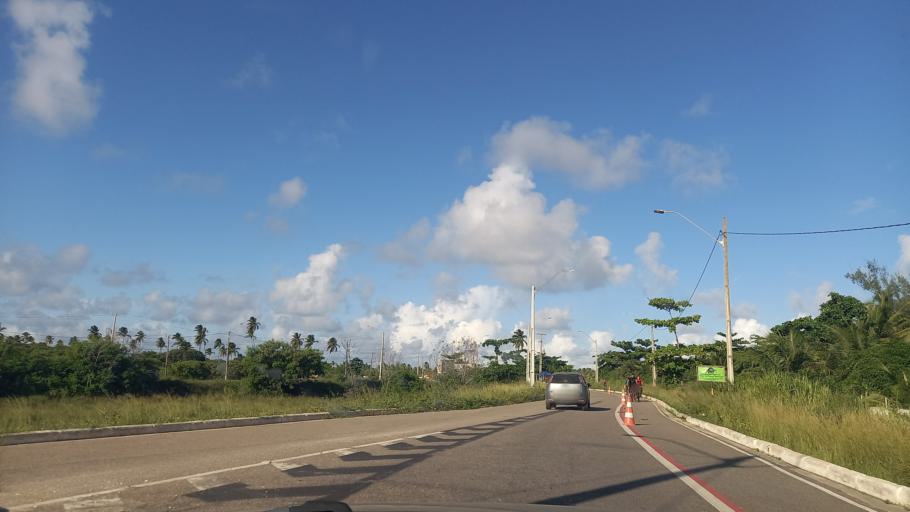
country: BR
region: Pernambuco
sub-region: Jaboatao Dos Guararapes
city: Jaboatao
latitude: -8.2382
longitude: -34.9388
